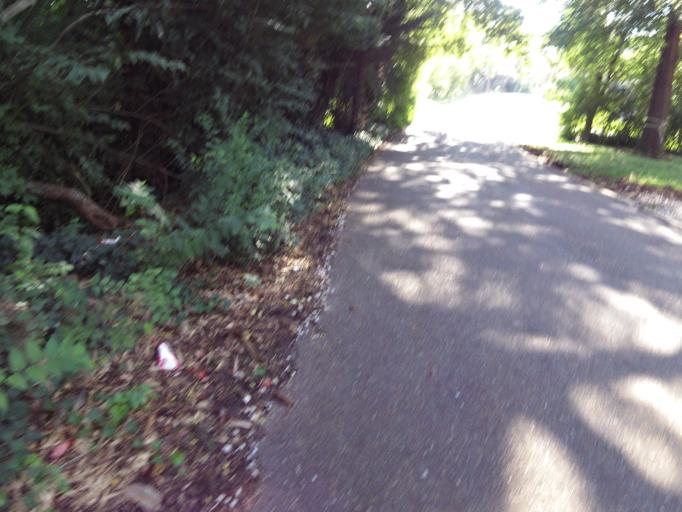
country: US
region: Tennessee
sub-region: Knox County
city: Knoxville
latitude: 35.9381
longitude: -83.9645
